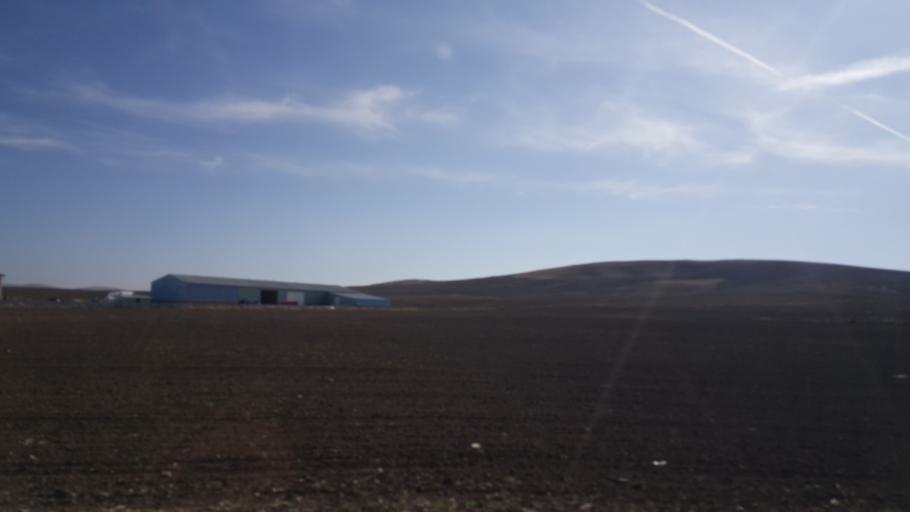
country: TR
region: Ankara
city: Yenice
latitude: 39.3726
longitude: 32.7249
